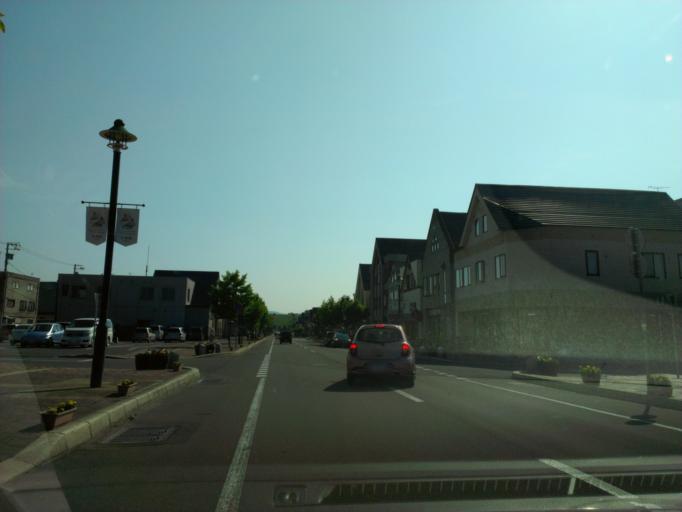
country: JP
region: Hokkaido
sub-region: Asahikawa-shi
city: Asahikawa
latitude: 43.5916
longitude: 142.4639
